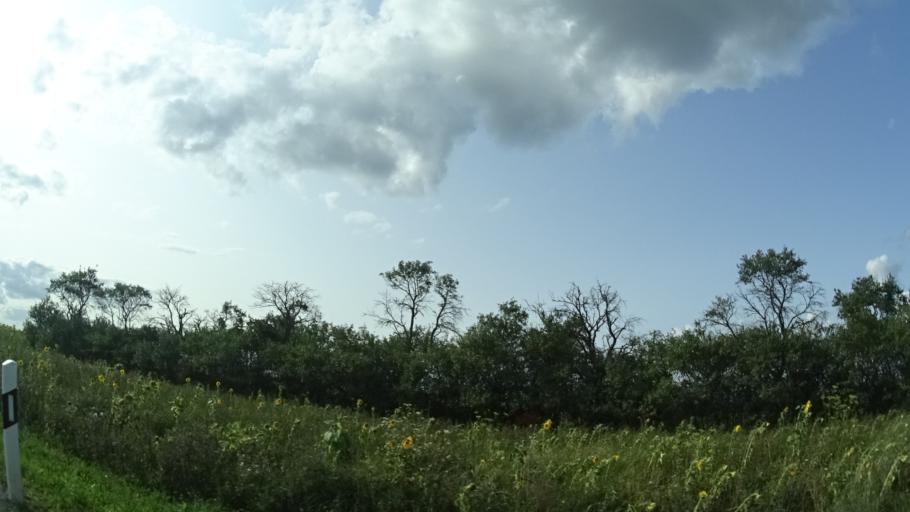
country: DE
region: Baden-Wuerttemberg
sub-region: Regierungsbezirk Stuttgart
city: Kulsheim
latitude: 49.6790
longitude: 9.5447
